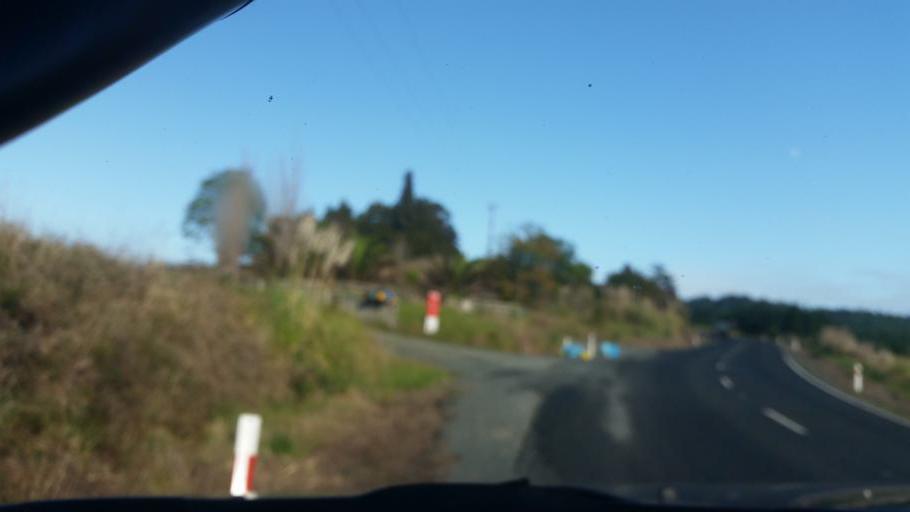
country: NZ
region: Auckland
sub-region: Auckland
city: Wellsford
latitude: -36.2212
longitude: 174.4612
